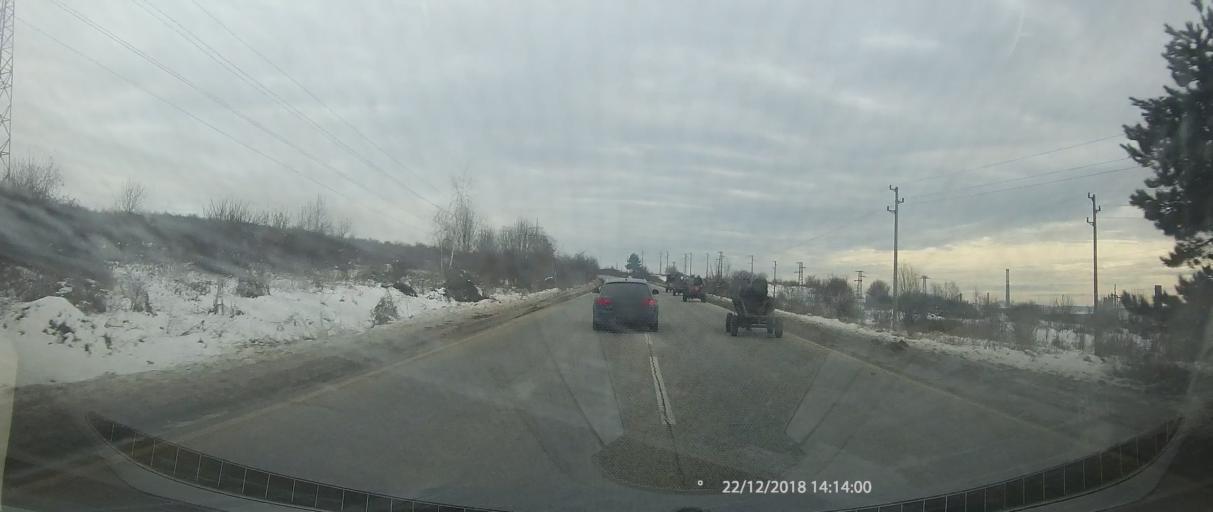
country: BG
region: Pleven
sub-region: Obshtina Pleven
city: Pleven
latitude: 43.4322
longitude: 24.6143
